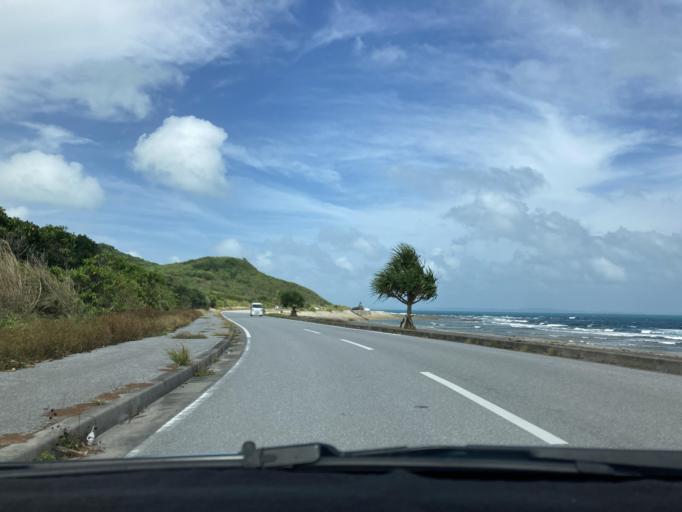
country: JP
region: Okinawa
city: Ginowan
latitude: 26.1840
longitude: 127.8216
